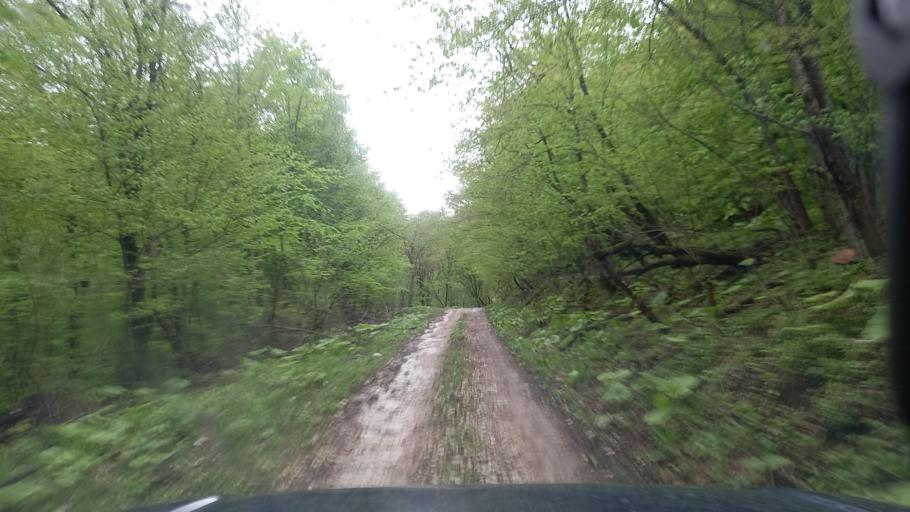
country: RU
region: Kabardino-Balkariya
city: Babugent
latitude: 43.2158
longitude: 43.5495
